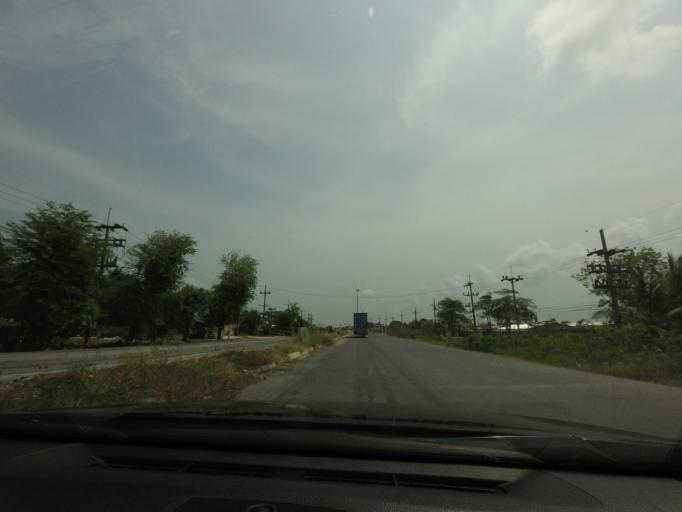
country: TH
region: Nakhon Si Thammarat
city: Hua Sai
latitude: 7.9333
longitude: 100.3337
